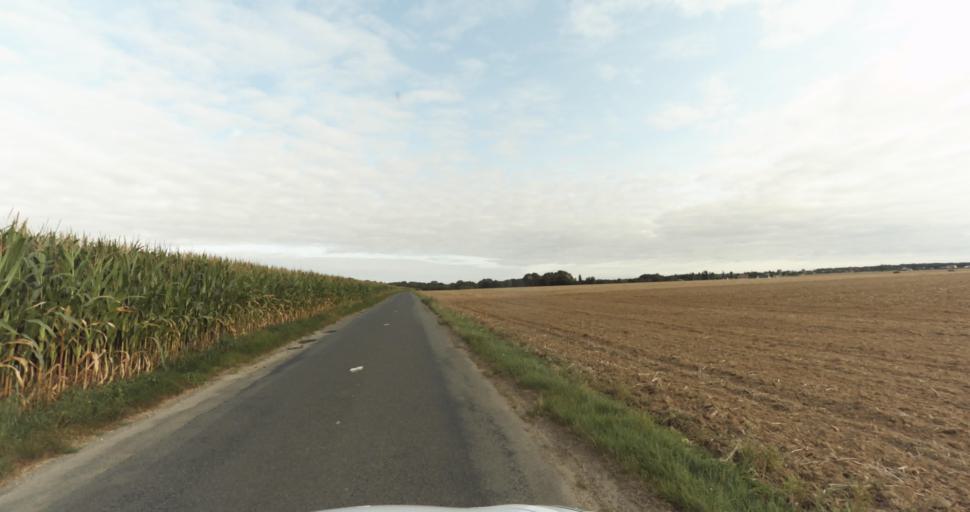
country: FR
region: Haute-Normandie
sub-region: Departement de l'Eure
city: Saint-Germain-sur-Avre
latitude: 48.8099
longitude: 1.2680
